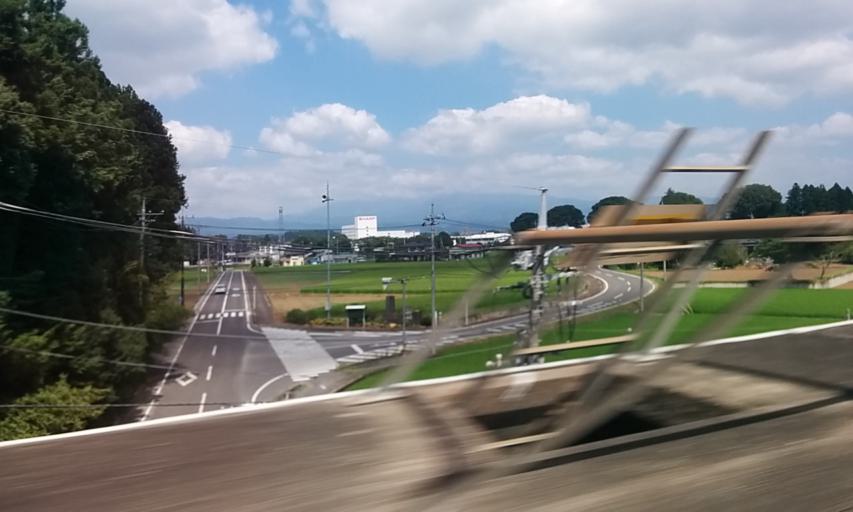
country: JP
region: Tochigi
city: Yaita
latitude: 36.7812
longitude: 139.9520
